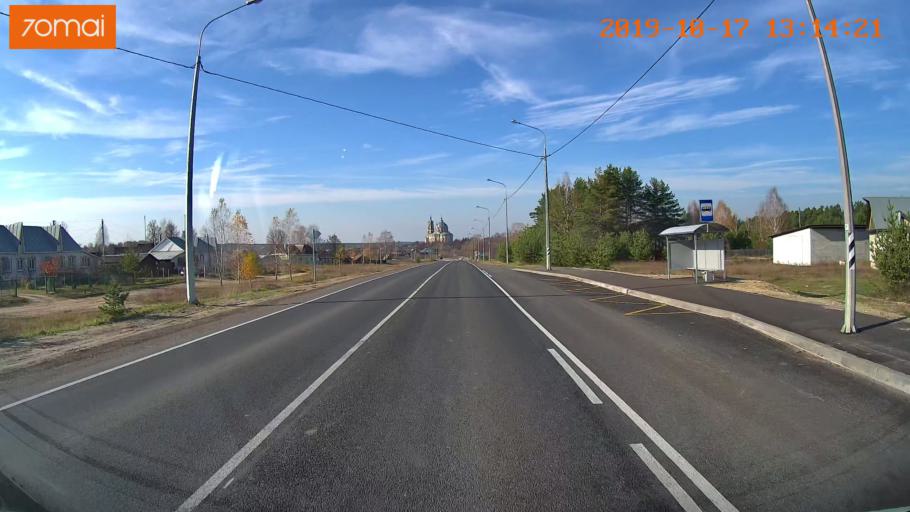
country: RU
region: Rjazan
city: Gus'-Zheleznyy
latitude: 55.0518
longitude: 41.1726
